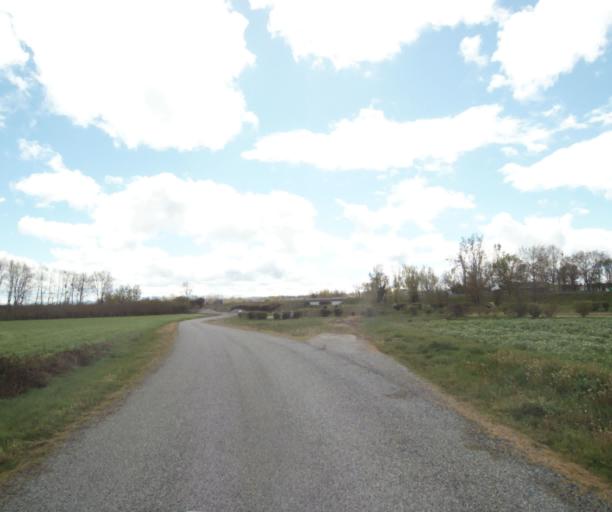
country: FR
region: Midi-Pyrenees
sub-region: Departement de l'Ariege
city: Saverdun
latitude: 43.2523
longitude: 1.5671
